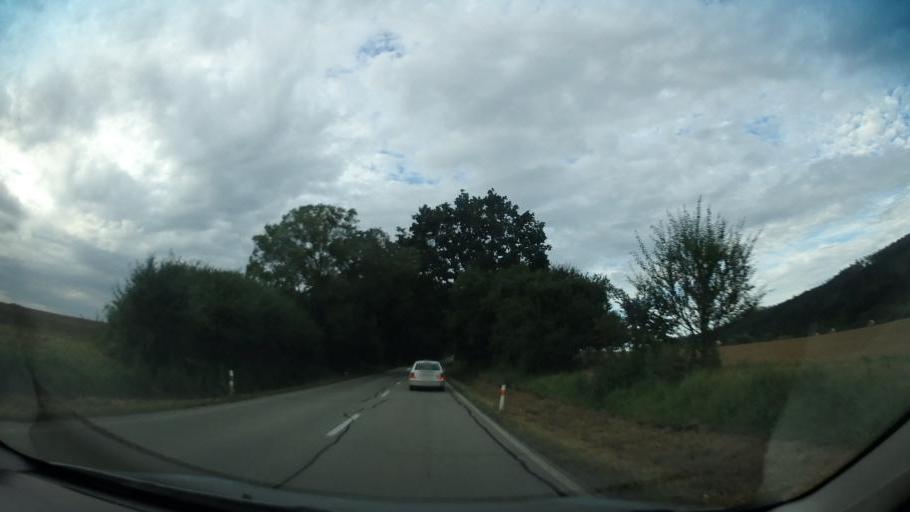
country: CZ
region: South Moravian
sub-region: Okres Blansko
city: Boskovice
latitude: 49.5159
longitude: 16.6790
